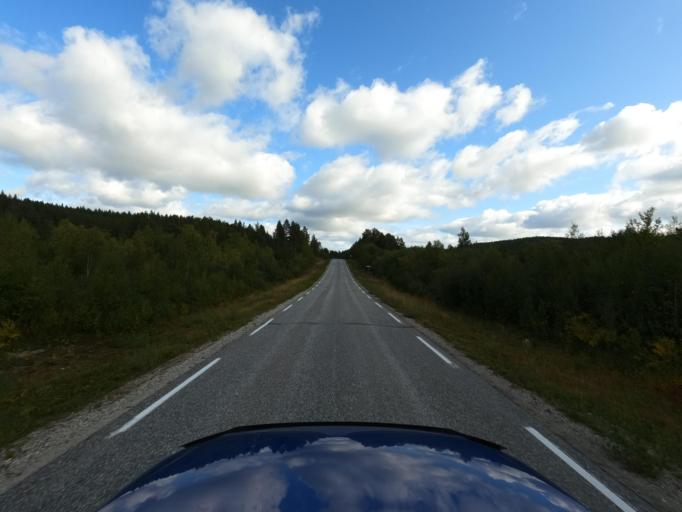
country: NO
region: Finnmark Fylke
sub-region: Karasjok
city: Karasjohka
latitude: 69.4349
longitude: 25.1550
